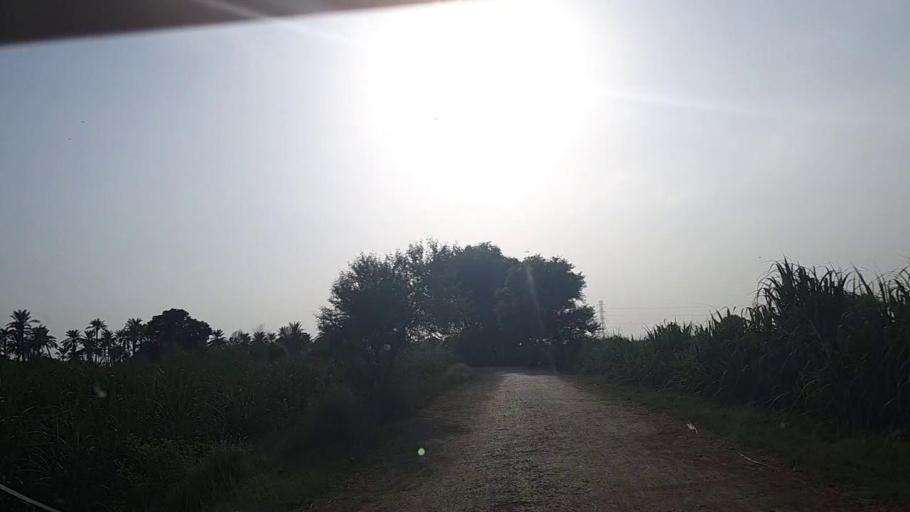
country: PK
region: Sindh
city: Ghotki
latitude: 27.9761
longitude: 69.2570
